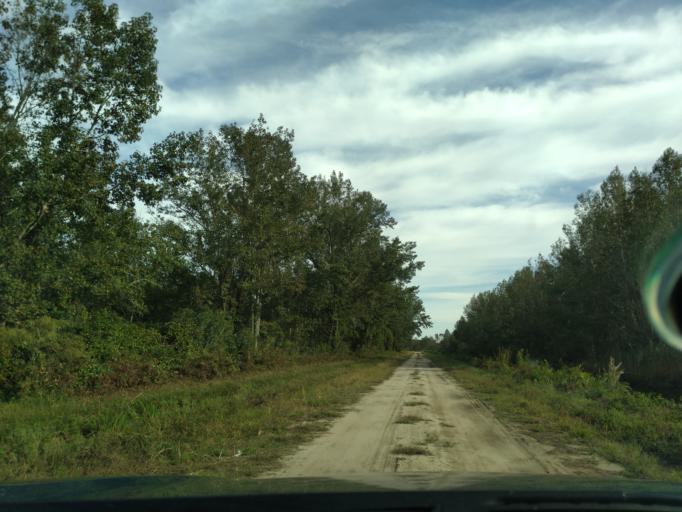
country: US
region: North Carolina
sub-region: Beaufort County
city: Belhaven
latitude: 35.6922
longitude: -76.5534
